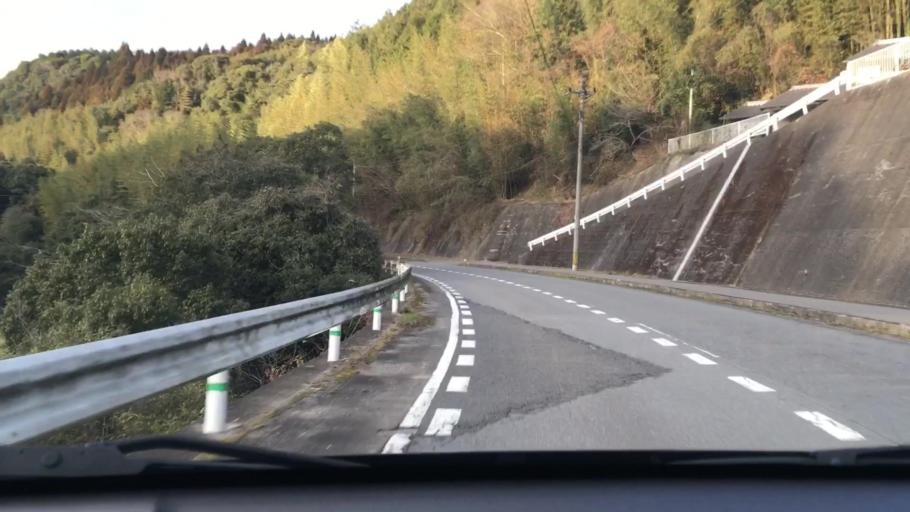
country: JP
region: Oita
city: Hiji
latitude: 33.4198
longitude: 131.4192
